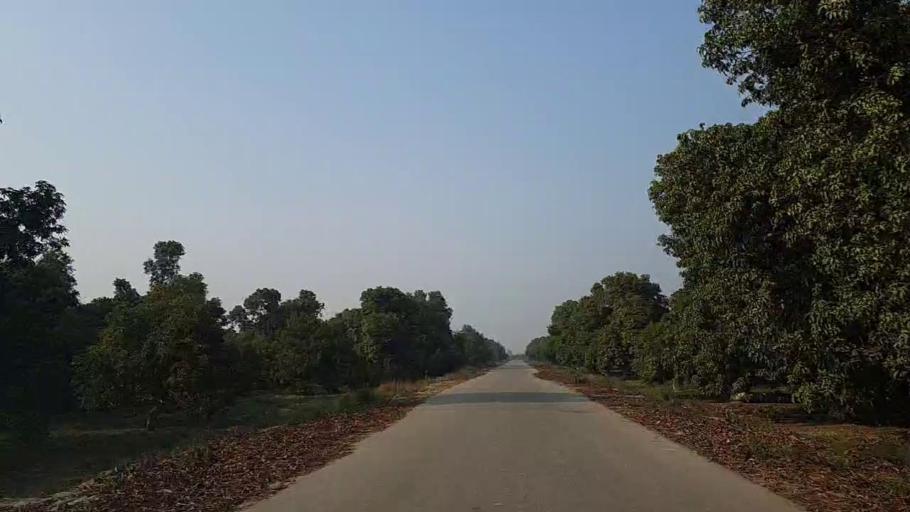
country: PK
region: Sindh
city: Sann
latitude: 26.1063
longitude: 68.1510
